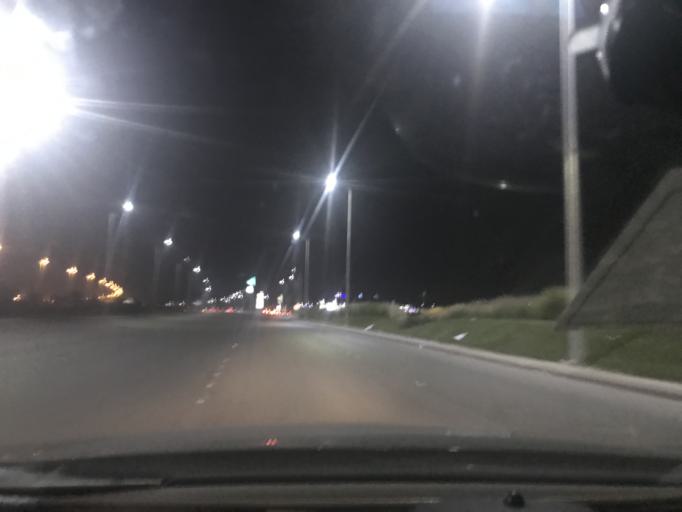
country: SA
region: Ar Riyad
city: Riyadh
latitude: 24.8439
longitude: 46.7320
